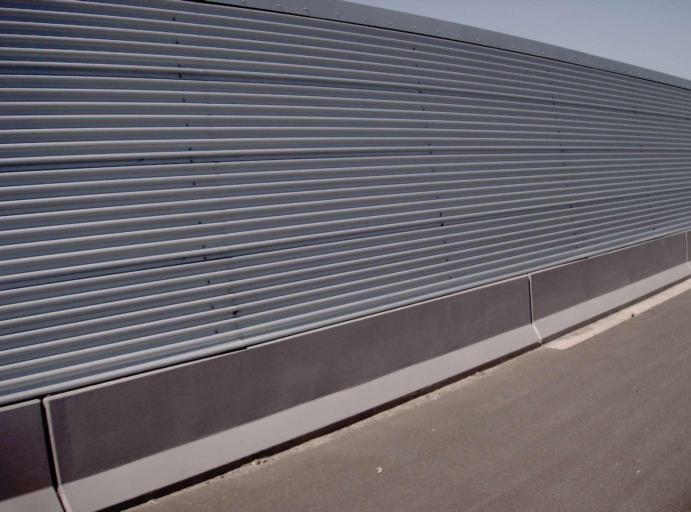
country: AU
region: Victoria
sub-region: Greater Dandenong
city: Keysborough
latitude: -37.9967
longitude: 145.1601
